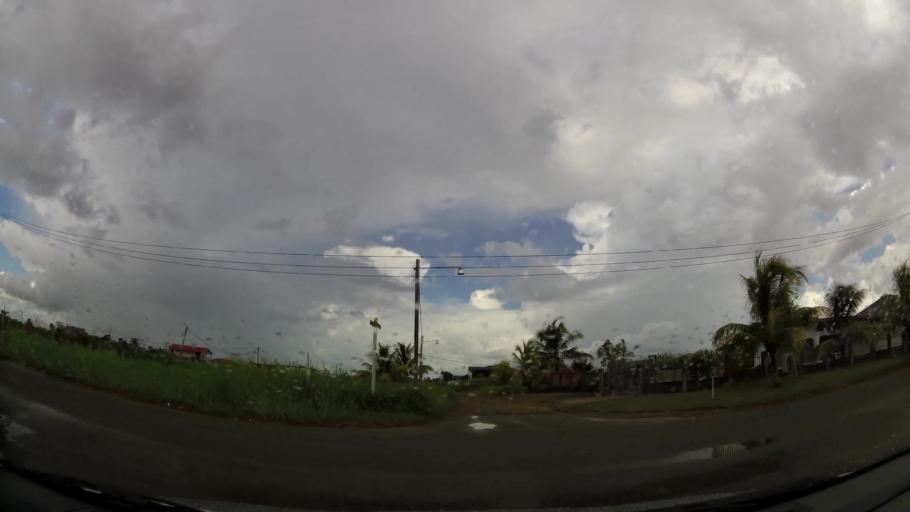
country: SR
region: Commewijne
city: Nieuw Amsterdam
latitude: 5.8627
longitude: -55.1146
